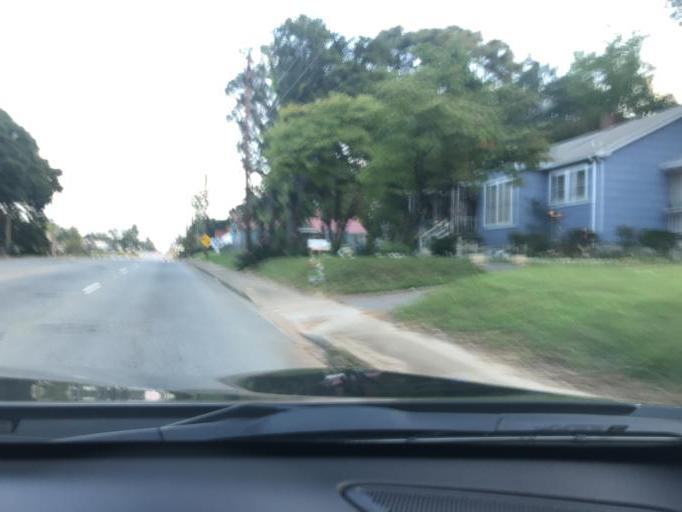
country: US
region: South Carolina
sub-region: Greenville County
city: Welcome
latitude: 34.8308
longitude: -82.4387
